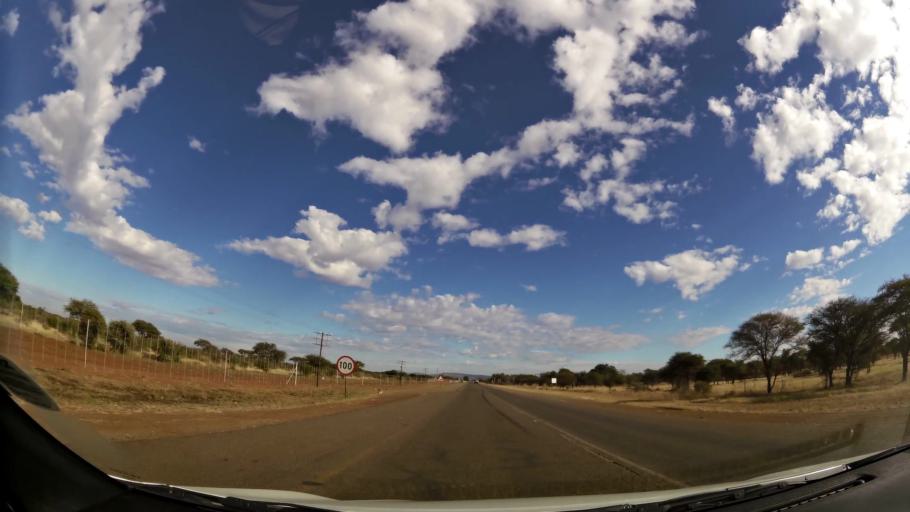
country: ZA
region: Limpopo
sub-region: Waterberg District Municipality
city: Bela-Bela
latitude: -24.9166
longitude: 28.3670
